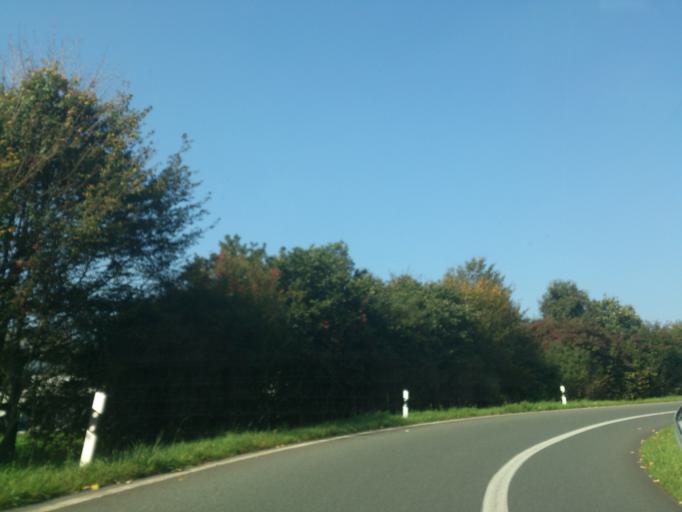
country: DE
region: North Rhine-Westphalia
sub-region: Regierungsbezirk Detmold
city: Paderborn
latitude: 51.7080
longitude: 8.7158
